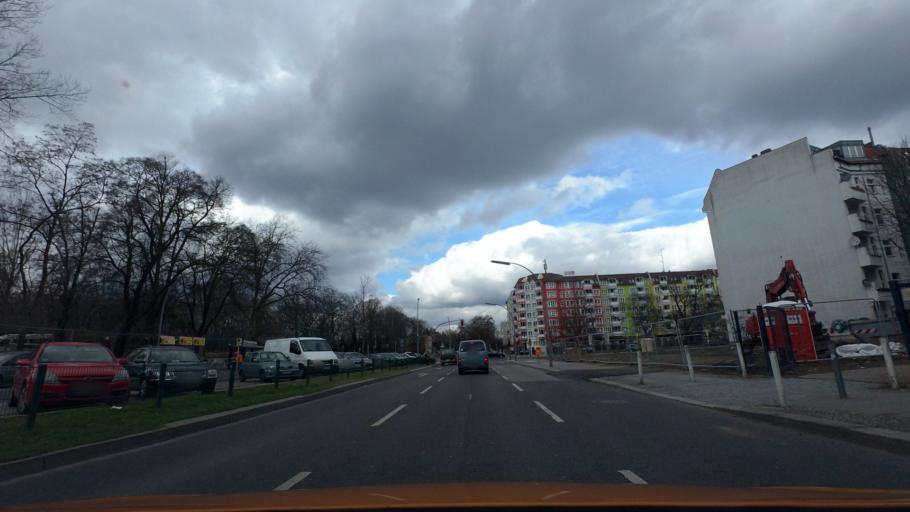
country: DE
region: Berlin
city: Wedding Bezirk
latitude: 52.5456
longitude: 13.3450
